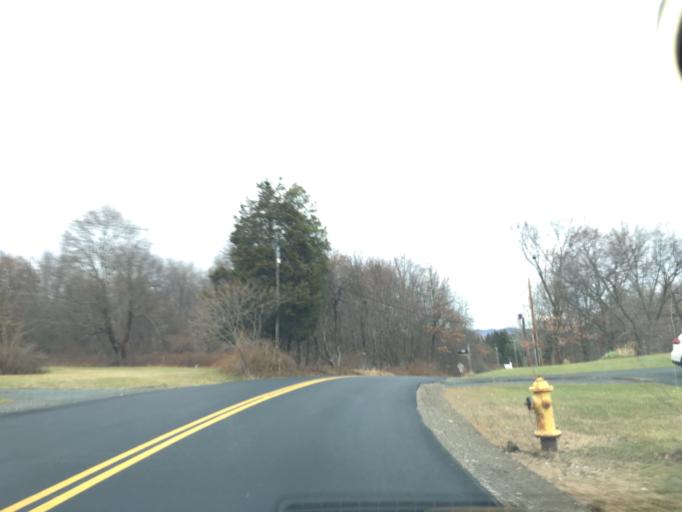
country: US
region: New York
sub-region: Rensselaer County
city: Wynantskill
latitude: 42.6694
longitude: -73.6437
